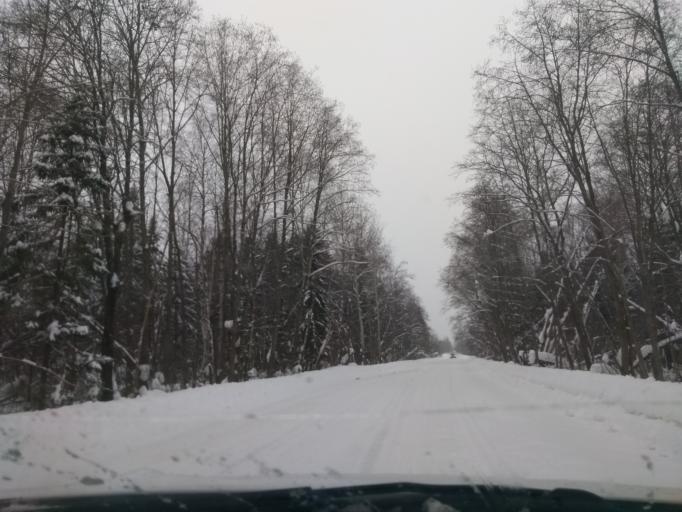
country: RU
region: Perm
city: Sylva
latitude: 57.8322
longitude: 56.6904
